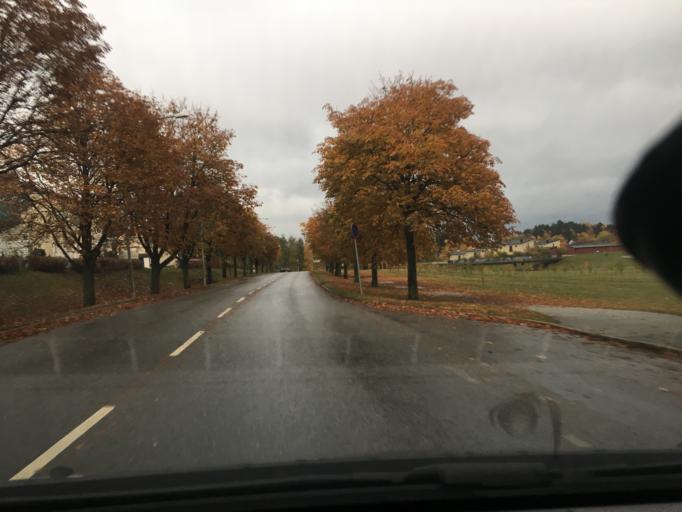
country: SE
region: Stockholm
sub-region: Stockholms Kommun
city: Kista
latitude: 59.3891
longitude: 17.9069
